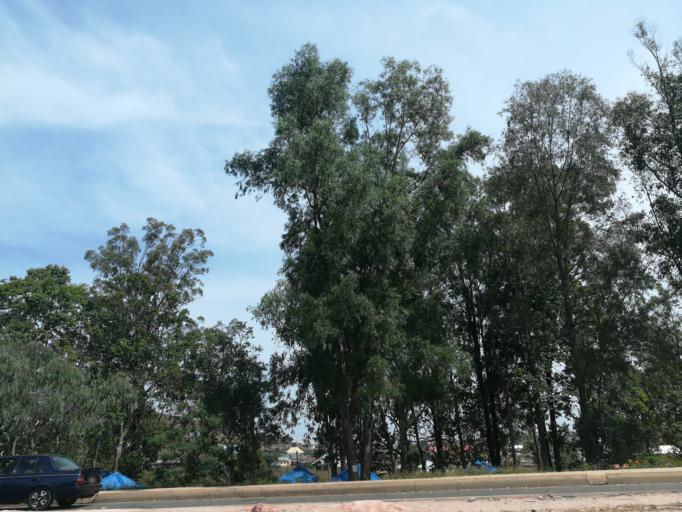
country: NG
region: Plateau
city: Bukuru
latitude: 9.8420
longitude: 8.8661
